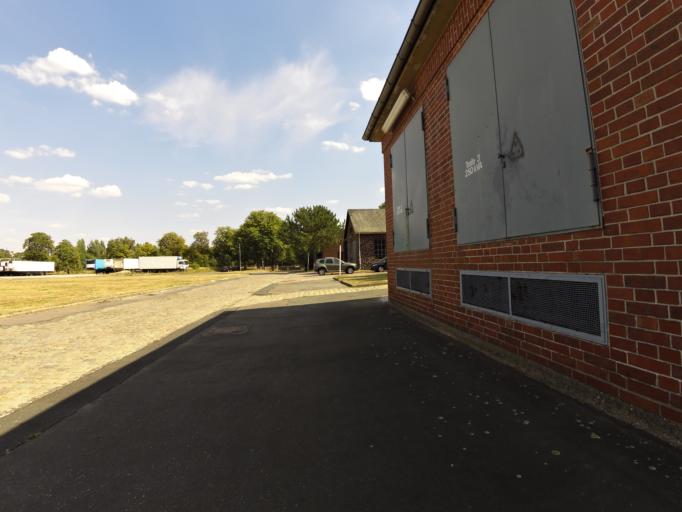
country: DE
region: Berlin
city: Mariendorf
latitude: 52.4386
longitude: 13.3705
